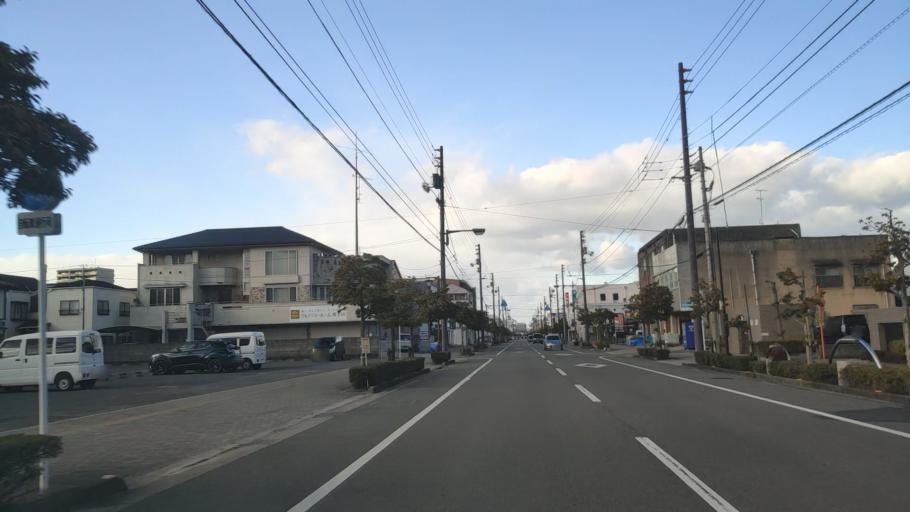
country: JP
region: Ehime
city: Saijo
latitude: 33.9147
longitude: 133.1867
